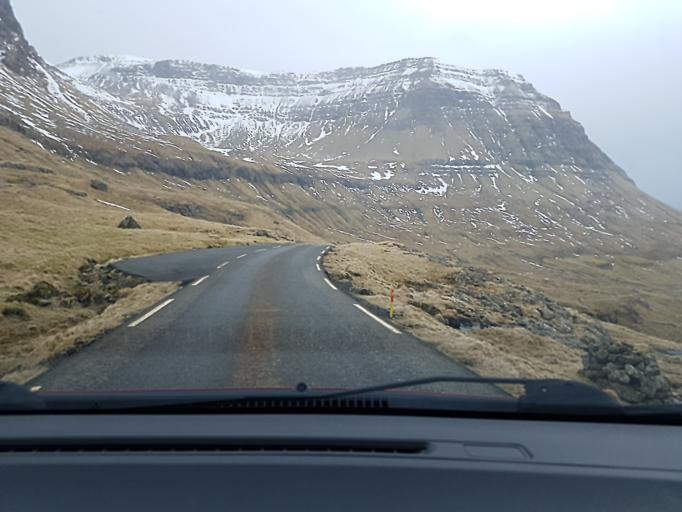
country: FO
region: Streymoy
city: Kollafjordhur
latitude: 62.0478
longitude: -6.9229
